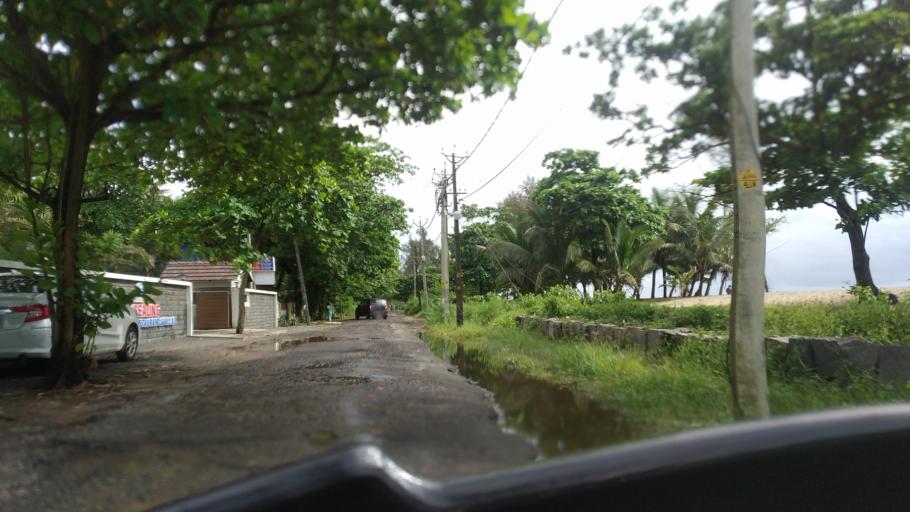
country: IN
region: Kerala
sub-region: Thrissur District
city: Kodungallur
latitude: 10.1296
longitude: 76.1824
